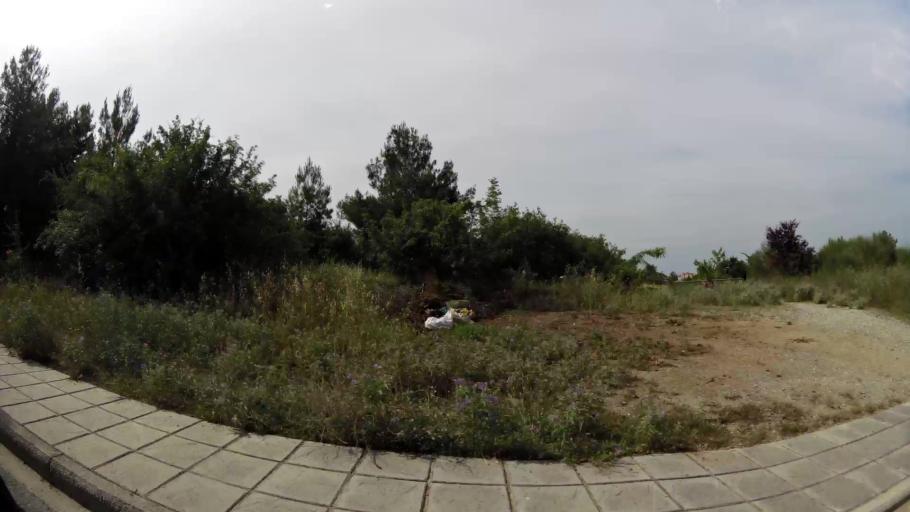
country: GR
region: Central Macedonia
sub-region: Nomos Thessalonikis
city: Panorama
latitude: 40.5816
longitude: 23.0171
